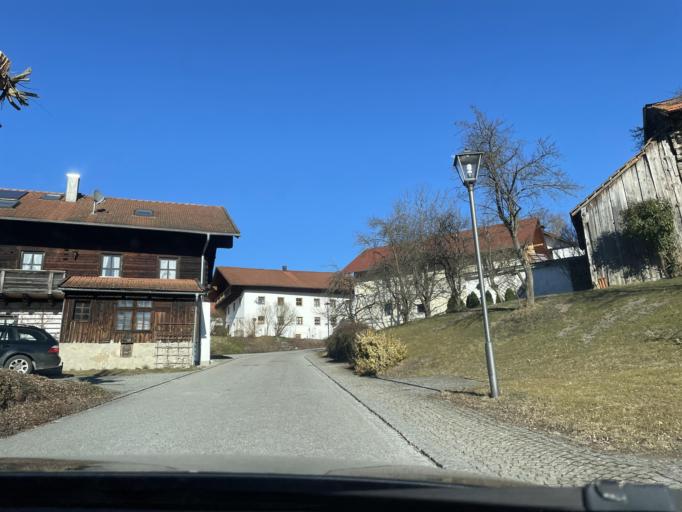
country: DE
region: Bavaria
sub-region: Lower Bavaria
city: Geiersthal
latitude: 49.0714
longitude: 12.9484
